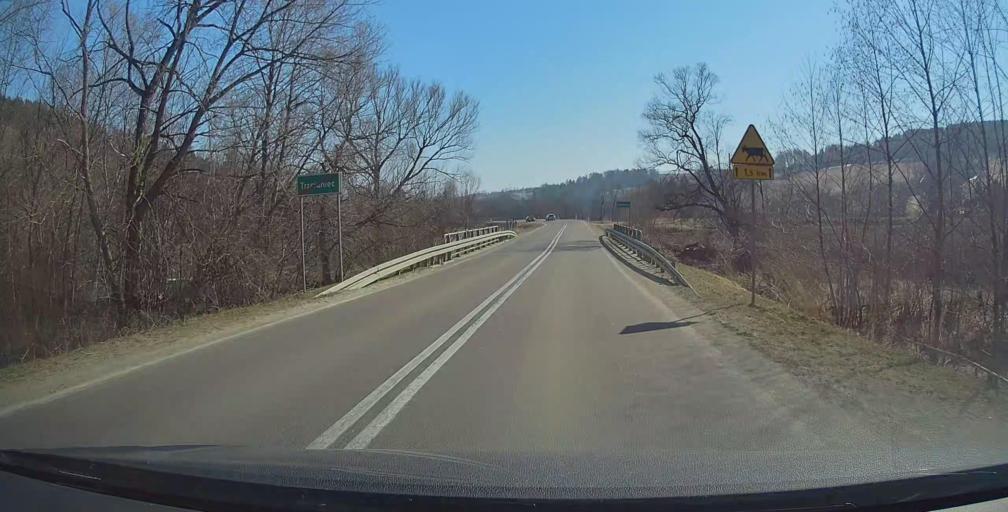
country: PL
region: Subcarpathian Voivodeship
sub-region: Powiat przemyski
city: Bircza
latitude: 49.5868
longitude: 22.5328
